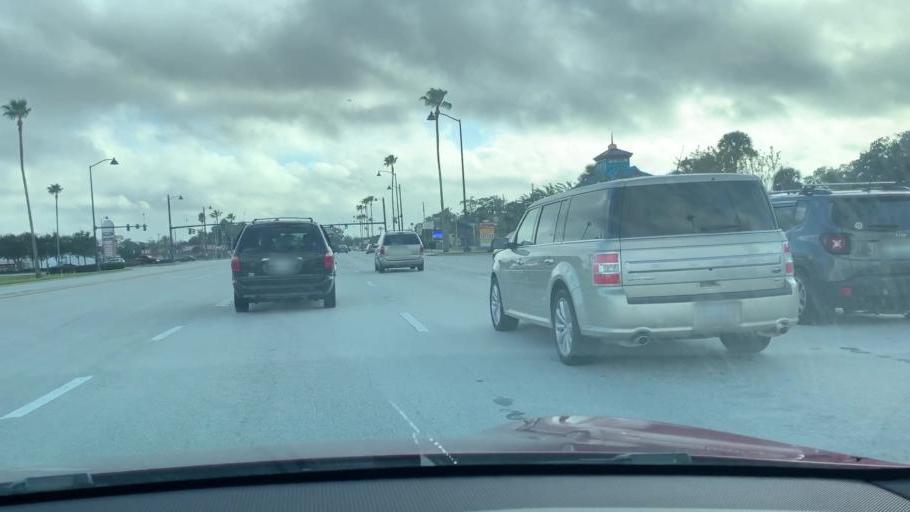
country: US
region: Florida
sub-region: Osceola County
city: Celebration
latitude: 28.3329
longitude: -81.4812
